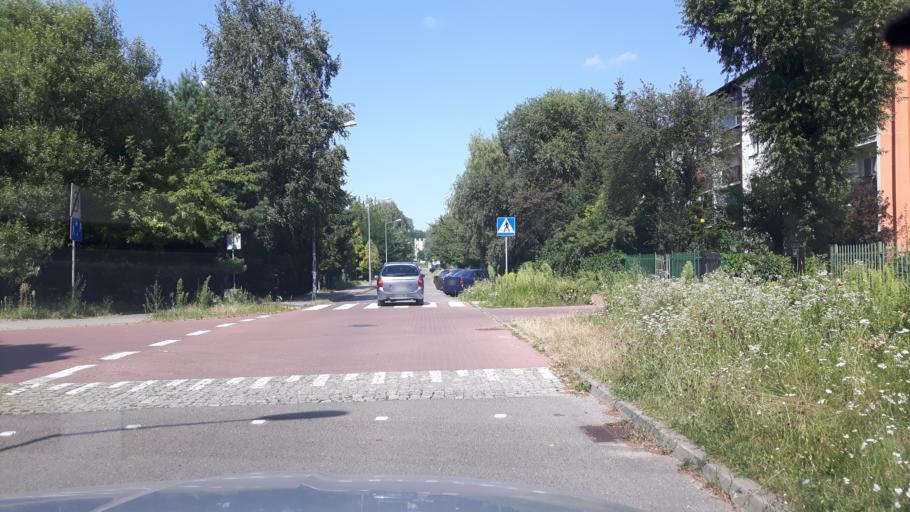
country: PL
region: Masovian Voivodeship
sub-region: Warszawa
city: Wesola
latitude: 52.2200
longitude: 21.2279
